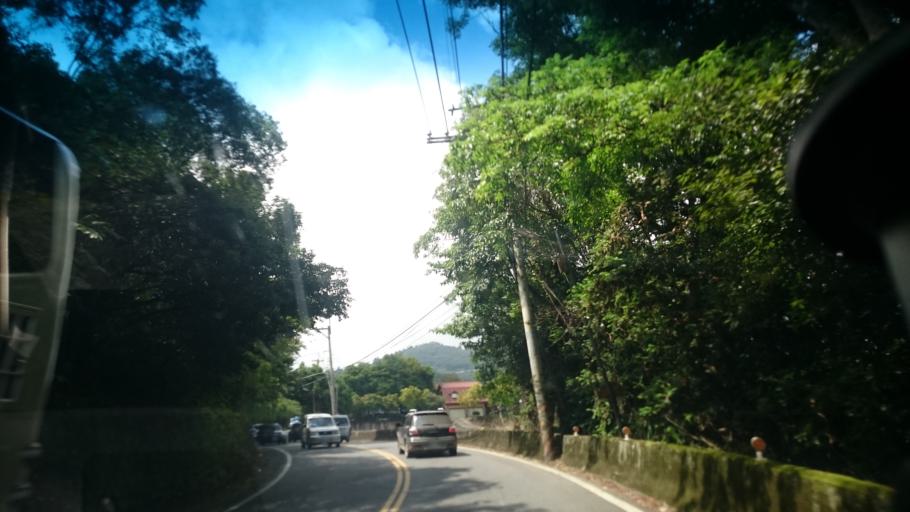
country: TW
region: Taiwan
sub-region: Nantou
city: Puli
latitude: 24.0398
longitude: 121.1582
